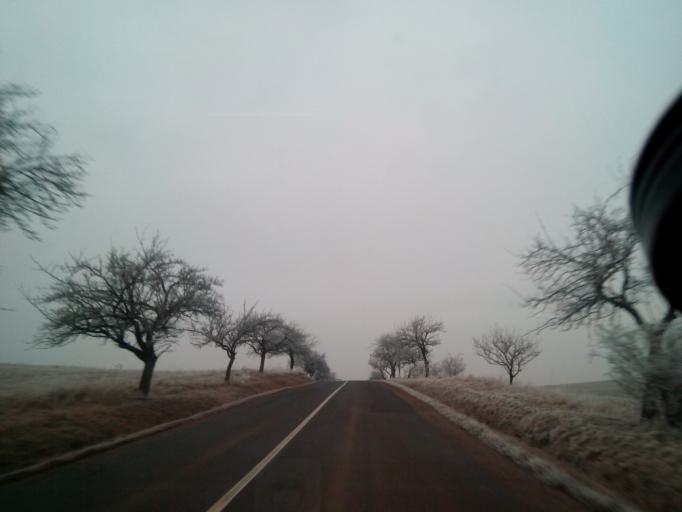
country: SK
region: Presovsky
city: Lubica
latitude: 48.9836
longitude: 20.4202
